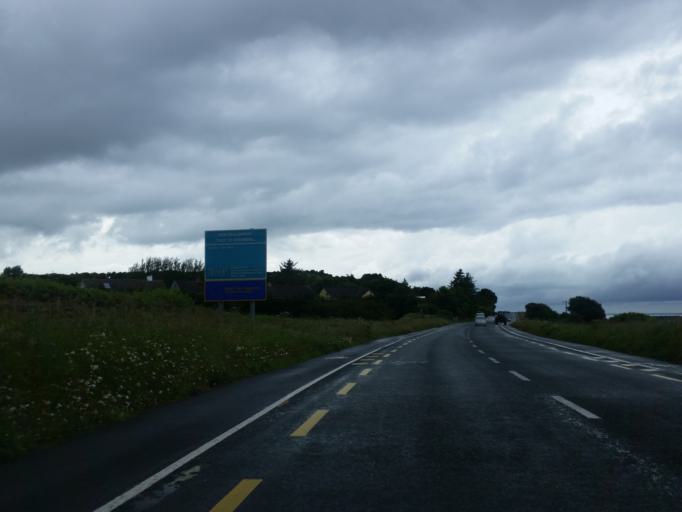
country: IE
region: Connaught
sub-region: Sligo
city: Strandhill
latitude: 54.2728
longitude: -8.5605
